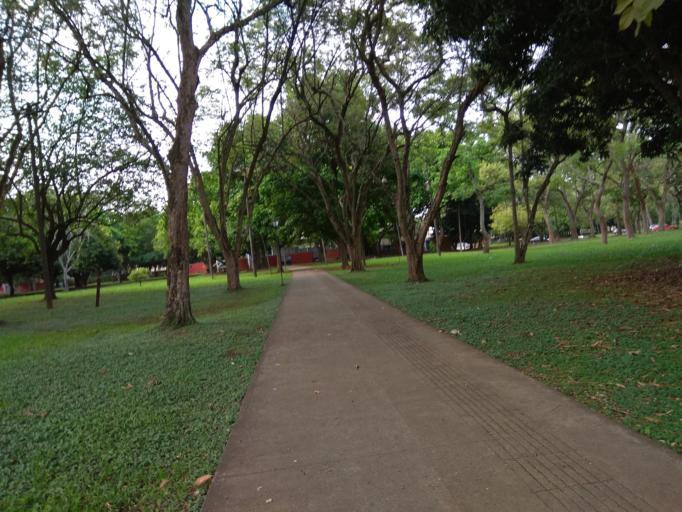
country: CO
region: Valle del Cauca
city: Cali
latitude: 3.3732
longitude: -76.5318
